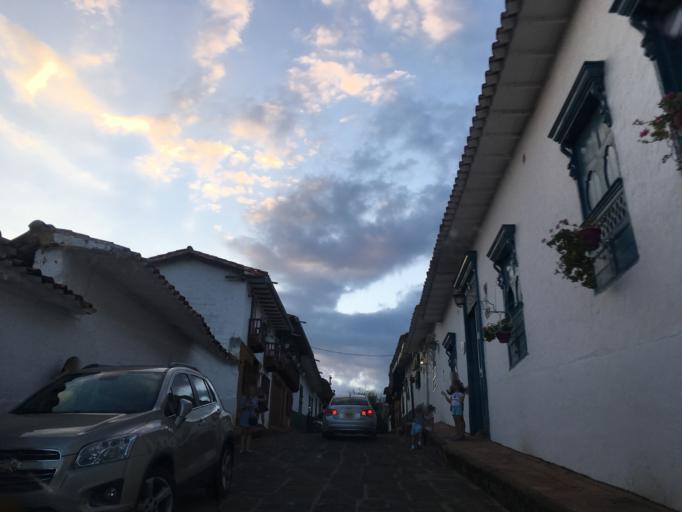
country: CO
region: Santander
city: Barichara
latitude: 6.6361
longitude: -73.2247
